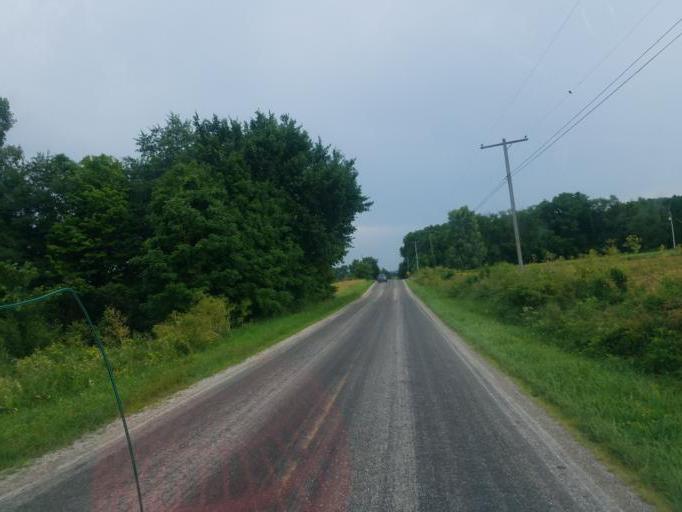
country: US
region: Ohio
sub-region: Wayne County
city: West Salem
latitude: 40.8740
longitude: -82.1550
